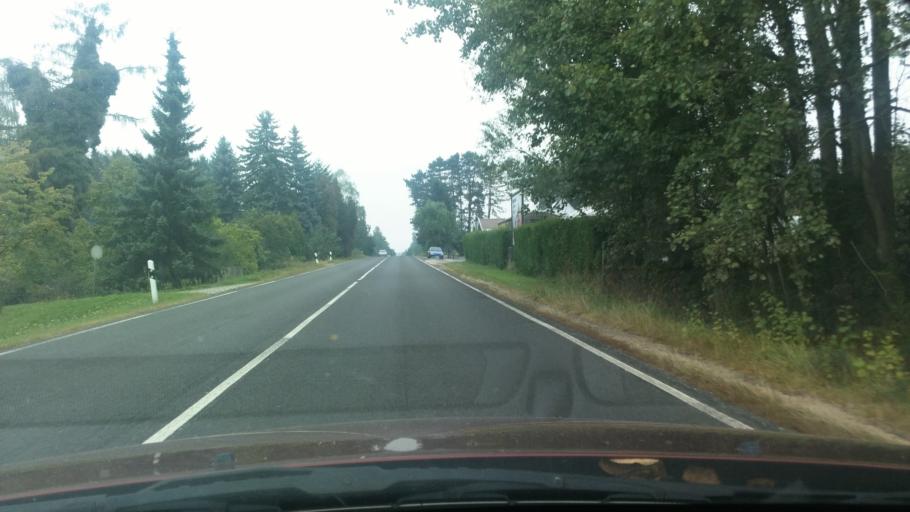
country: DE
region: Saxony
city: Goerlitz
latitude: 51.1709
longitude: 14.9683
